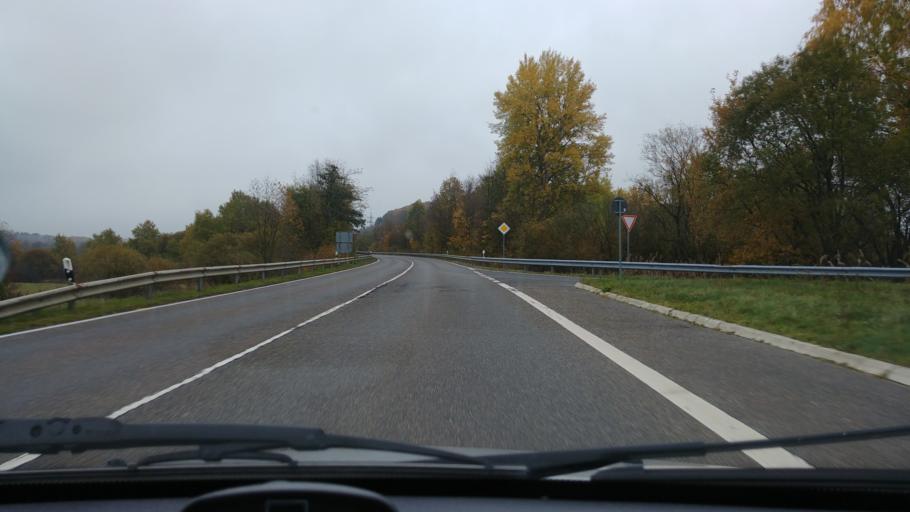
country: DE
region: Rheinland-Pfalz
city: Rotenhain
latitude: 50.6005
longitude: 7.8910
